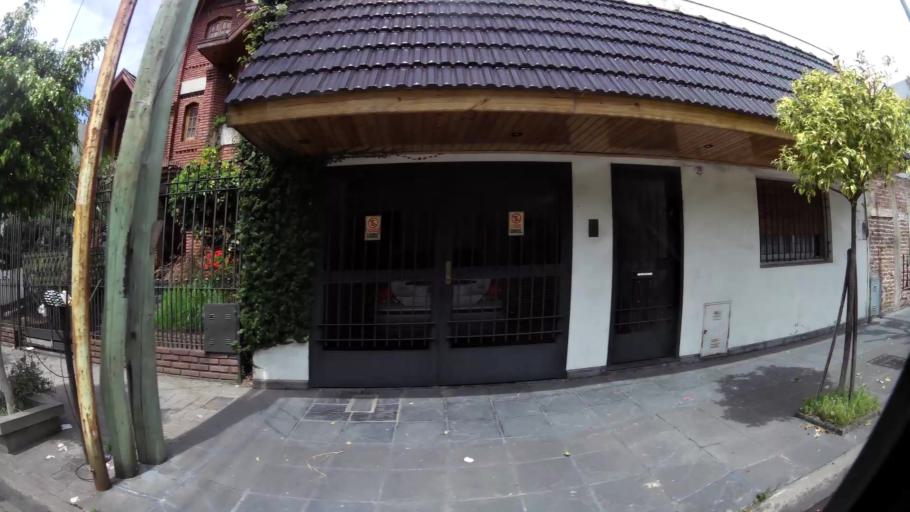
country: AR
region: Buenos Aires
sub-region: Partido de Lanus
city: Lanus
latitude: -34.6695
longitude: -58.4129
